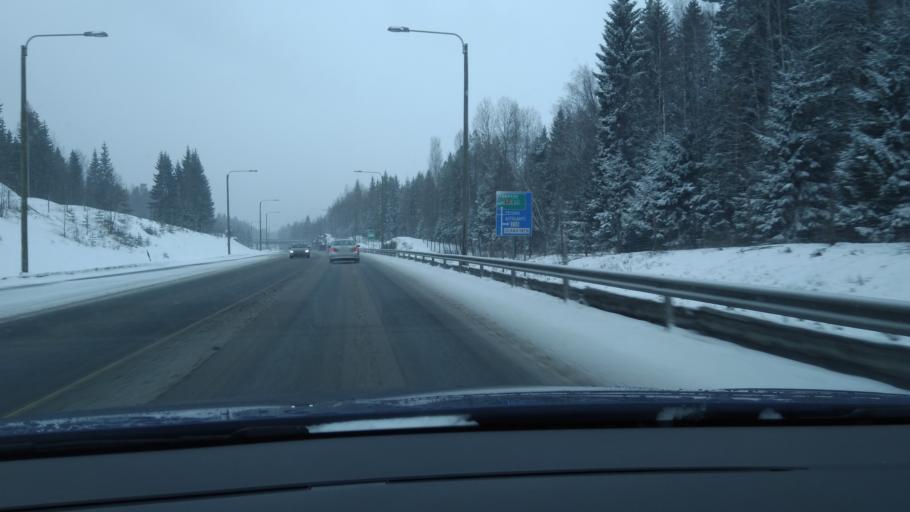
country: FI
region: Pirkanmaa
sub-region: Tampere
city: Kangasala
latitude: 61.5350
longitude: 23.9573
